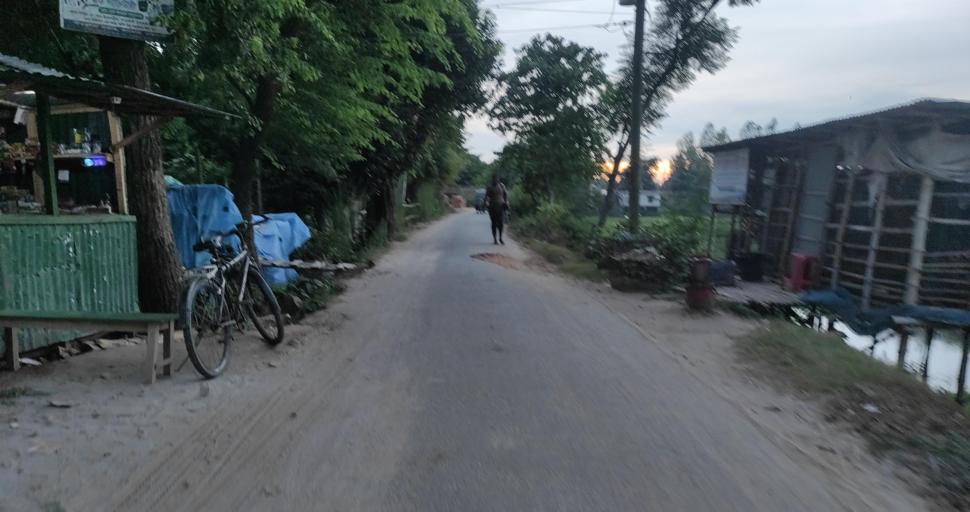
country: BD
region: Rajshahi
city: Par Naogaon
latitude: 24.5577
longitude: 88.9633
